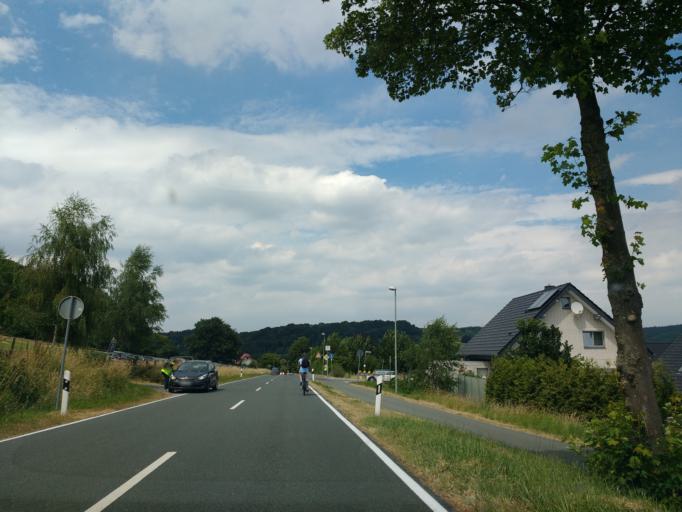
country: DE
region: North Rhine-Westphalia
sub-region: Regierungsbezirk Detmold
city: Altenbeken
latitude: 51.7562
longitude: 8.9427
